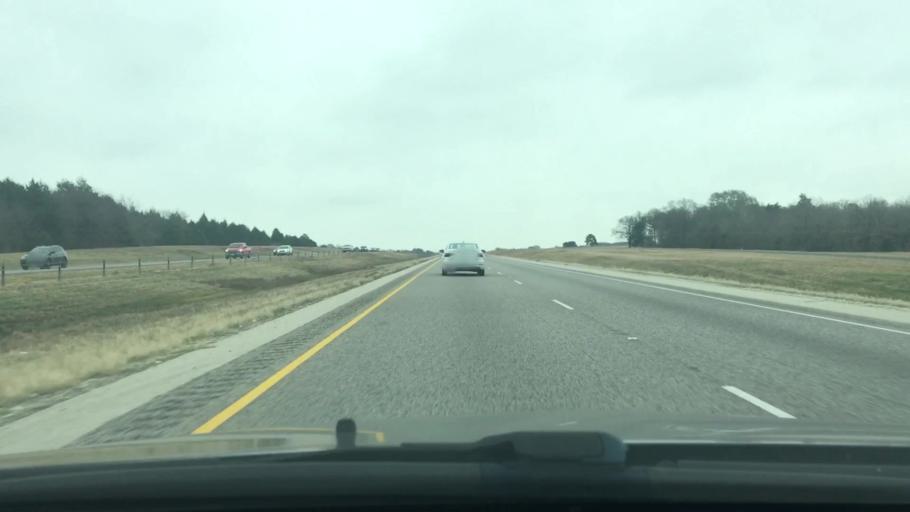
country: US
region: Texas
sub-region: Freestone County
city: Fairfield
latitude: 31.7868
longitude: -96.2421
